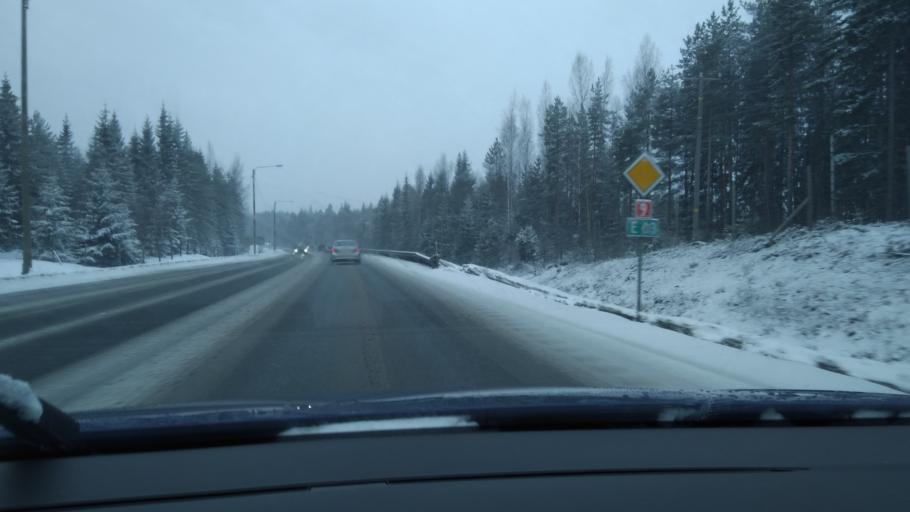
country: FI
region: Pirkanmaa
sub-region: Tampere
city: Kangasala
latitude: 61.5377
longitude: 23.9707
